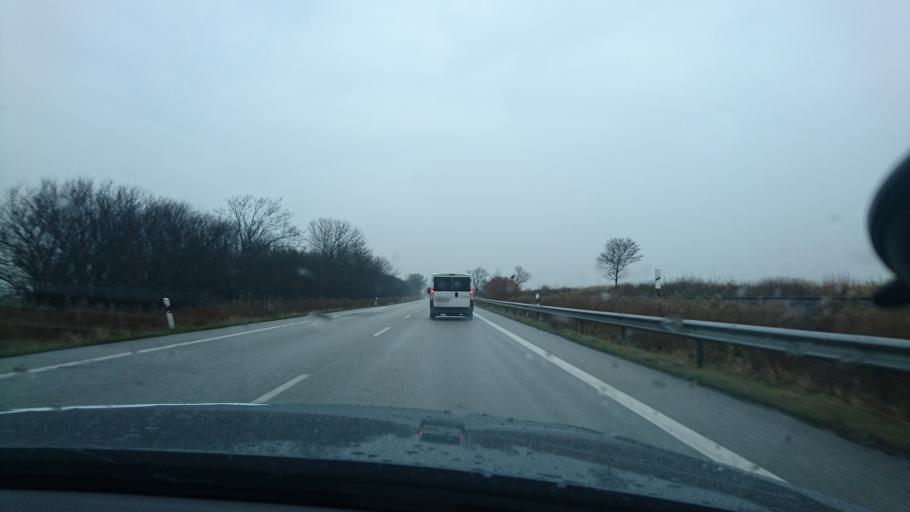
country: DE
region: Schleswig-Holstein
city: Fehmarn
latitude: 54.4393
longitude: 11.1579
